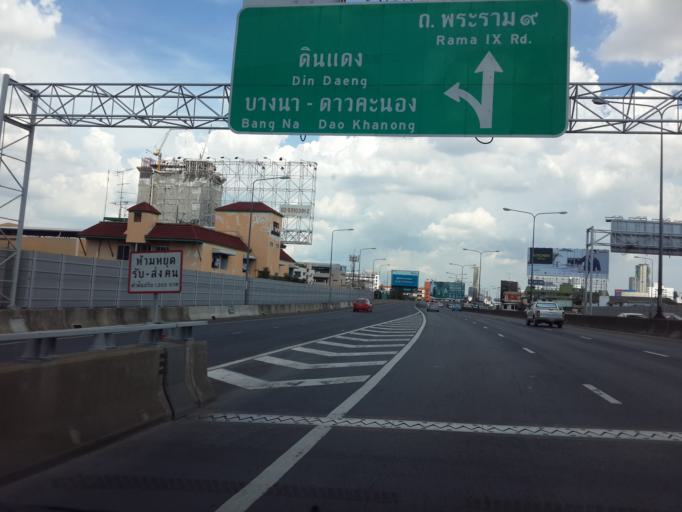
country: TH
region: Bangkok
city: Ratchathewi
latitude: 13.7644
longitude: 100.5416
